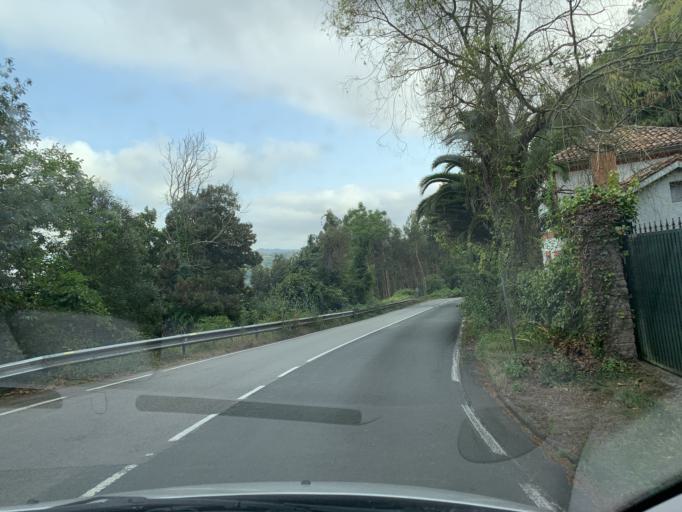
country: ES
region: Asturias
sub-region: Province of Asturias
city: Villaviciosa
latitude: 43.5088
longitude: -5.4266
